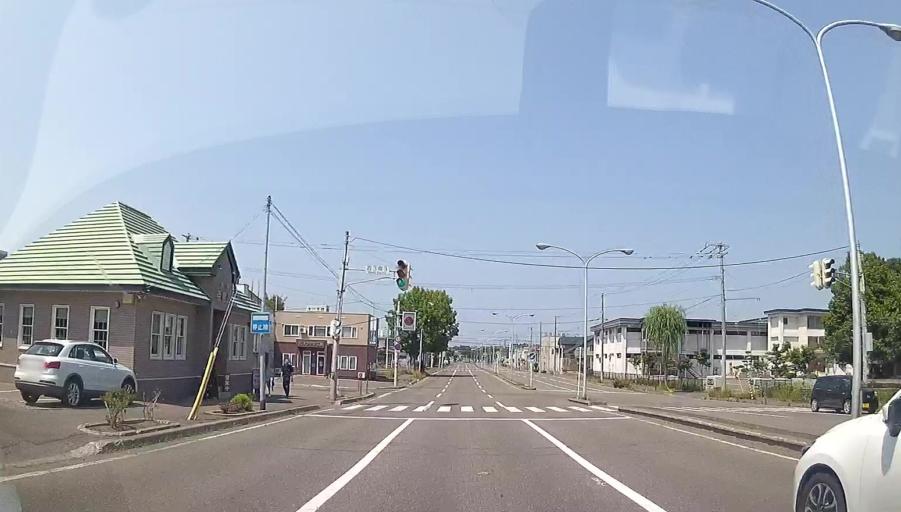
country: JP
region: Hokkaido
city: Obihiro
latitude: 42.9289
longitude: 143.1995
